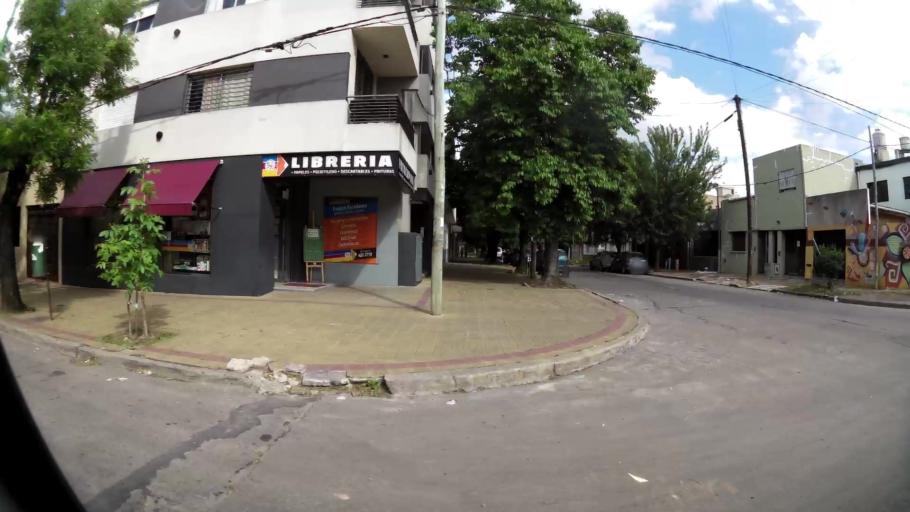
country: AR
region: Buenos Aires
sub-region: Partido de La Plata
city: La Plata
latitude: -34.9166
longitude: -57.9243
